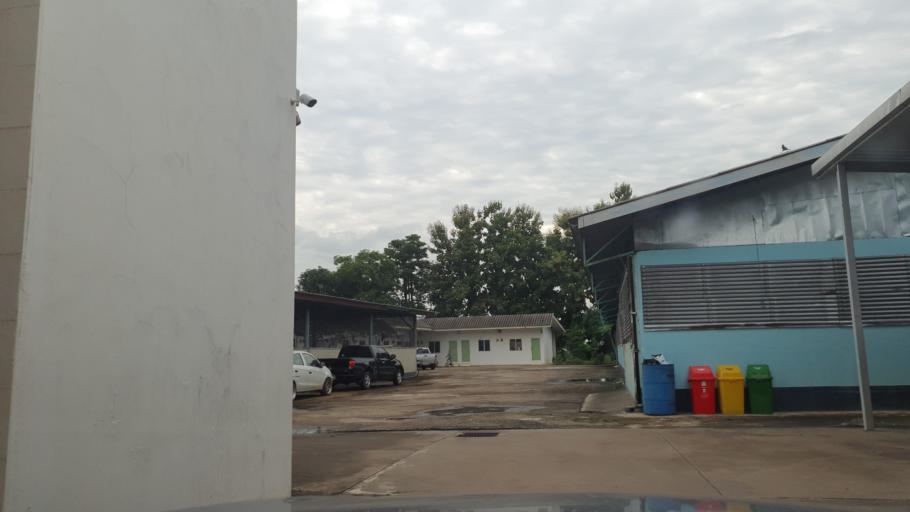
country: TH
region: Kamphaeng Phet
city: Kamphaeng Phet
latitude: 16.4385
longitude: 99.5106
